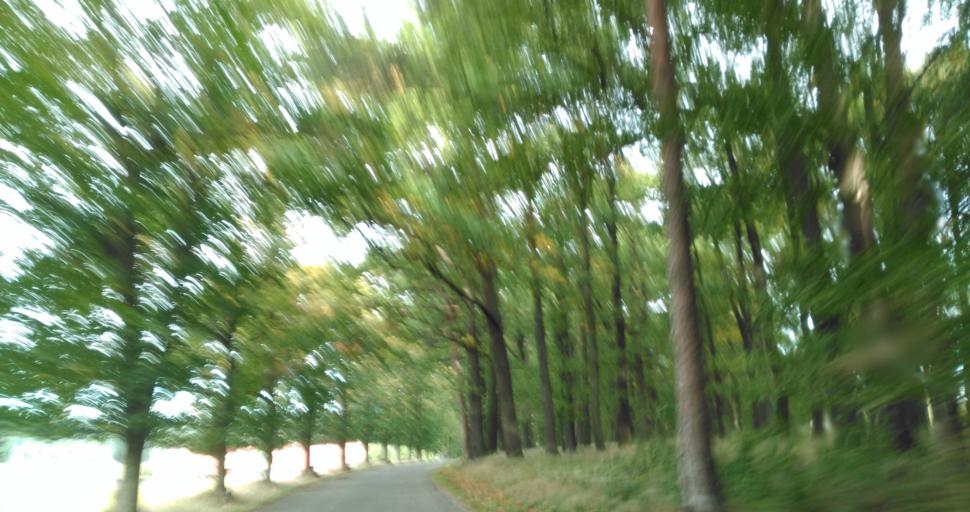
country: CZ
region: Plzensky
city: Zbiroh
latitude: 49.9191
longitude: 13.8211
